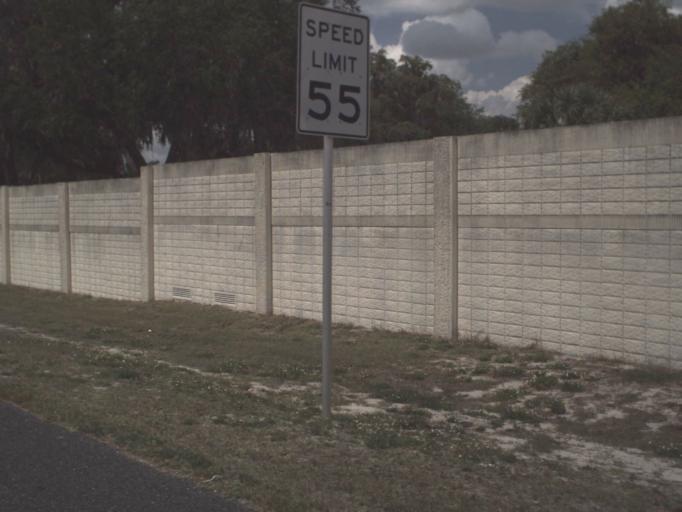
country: US
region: Florida
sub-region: Sumter County
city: Wildwood
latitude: 28.8241
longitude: -81.9806
